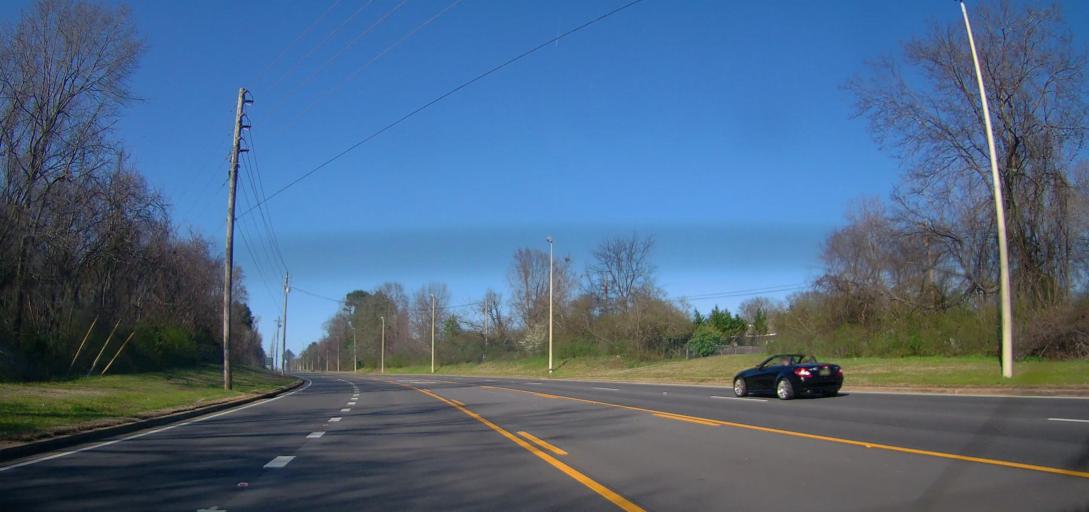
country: US
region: Alabama
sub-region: Lauderdale County
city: East Florence
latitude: 34.8151
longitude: -87.6268
